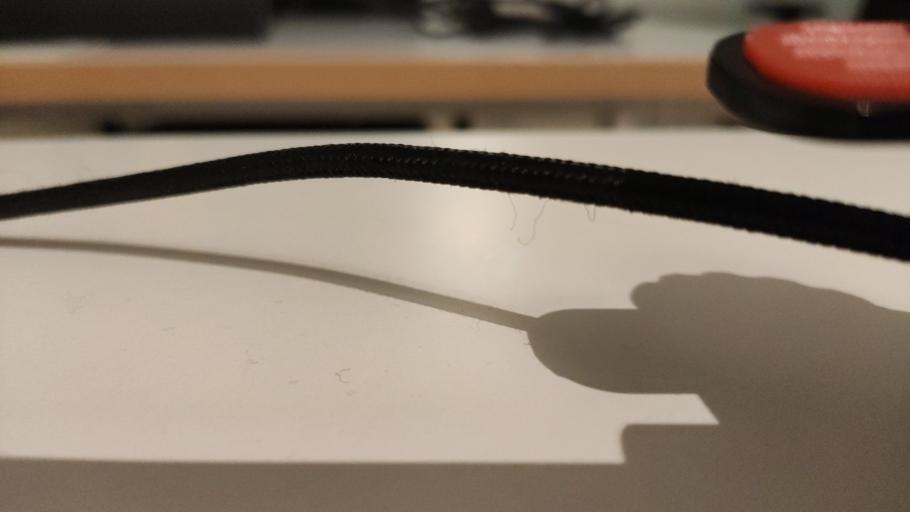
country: RU
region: Moskovskaya
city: Rogachevo
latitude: 56.4052
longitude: 37.2436
